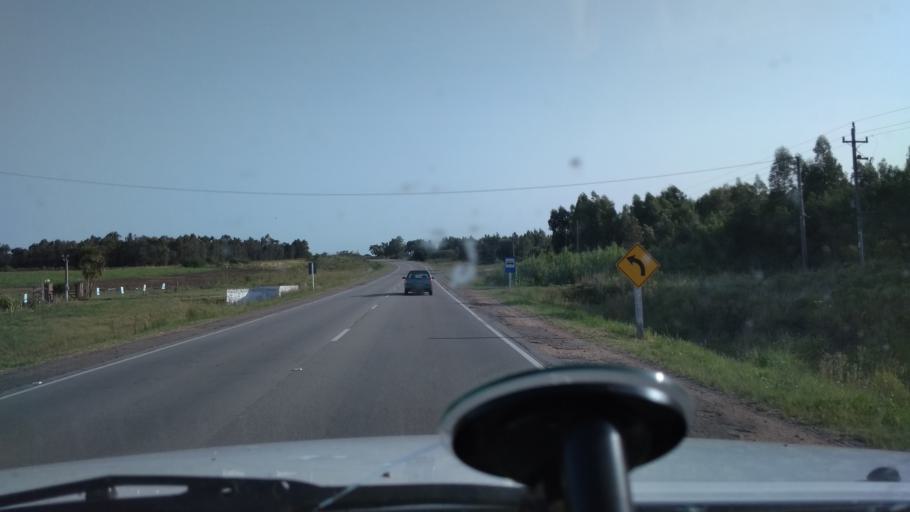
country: UY
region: Canelones
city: Sauce
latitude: -34.5762
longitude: -56.0572
